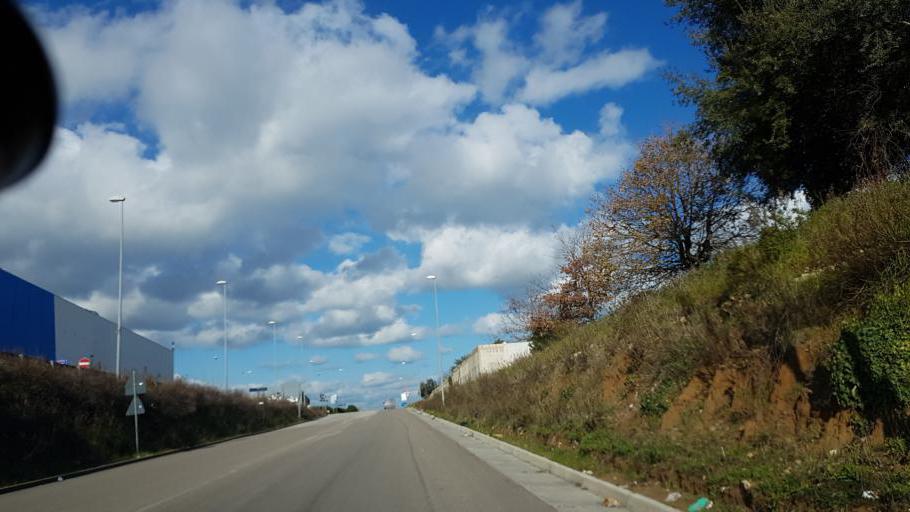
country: IT
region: Apulia
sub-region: Provincia di Brindisi
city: Brindisi
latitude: 40.6223
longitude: 17.9117
